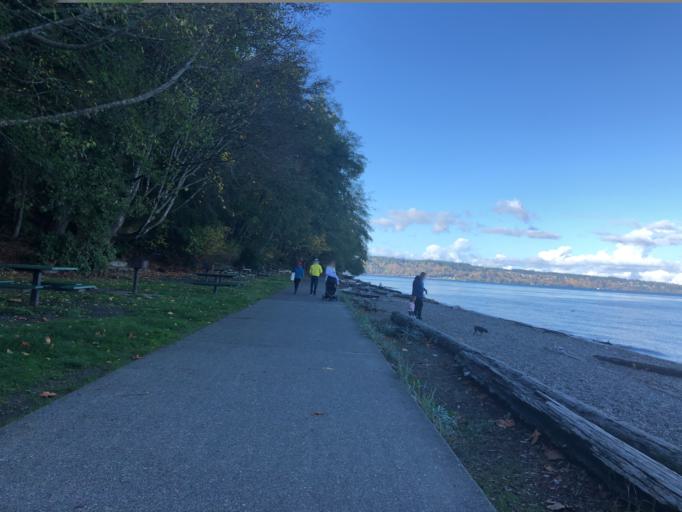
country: US
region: Washington
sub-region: Pierce County
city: Gig Harbor
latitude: 47.3140
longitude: -122.5298
